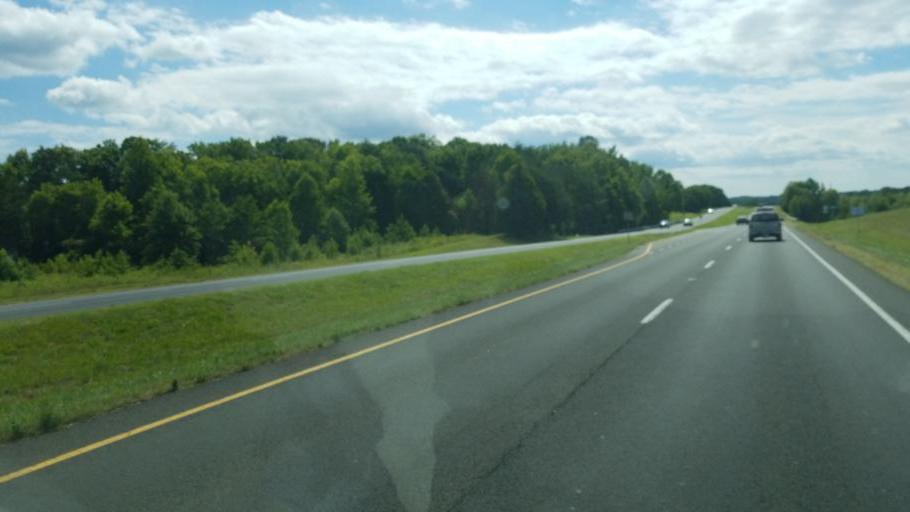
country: US
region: Virginia
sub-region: Fauquier County
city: Bealeton
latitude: 38.4439
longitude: -77.6497
